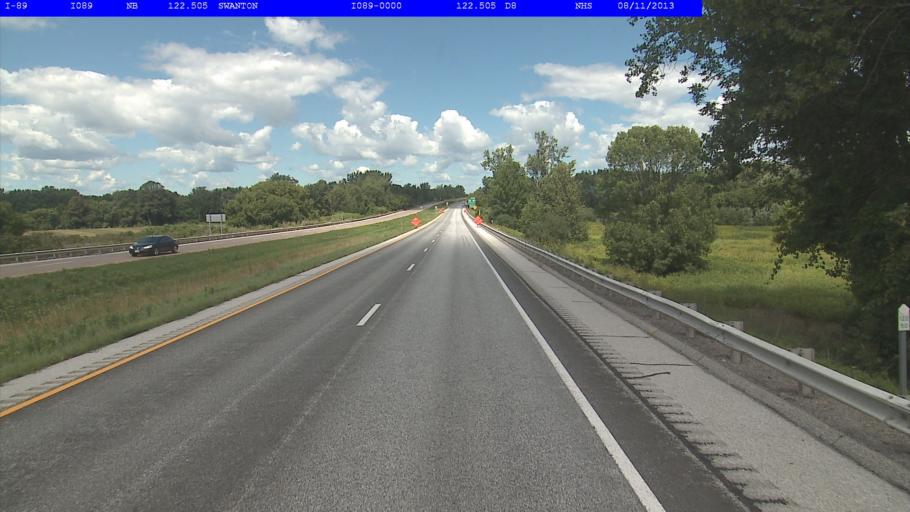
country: US
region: Vermont
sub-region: Franklin County
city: Swanton
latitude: 44.9107
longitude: -73.1007
